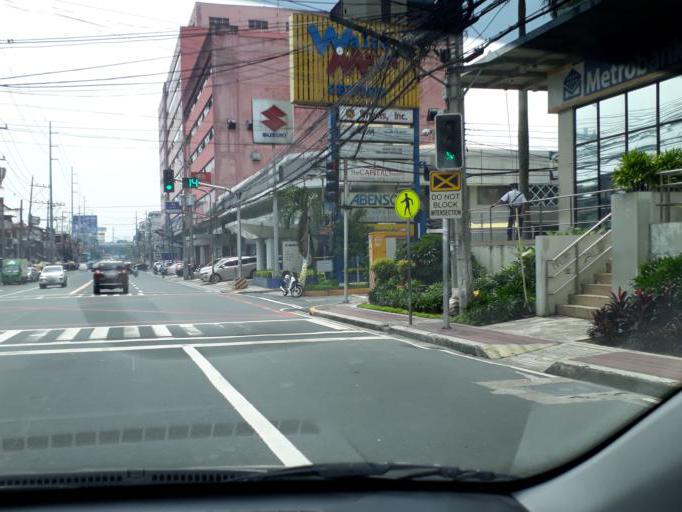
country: PH
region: Calabarzon
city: Del Monte
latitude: 14.6205
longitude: 121.0200
